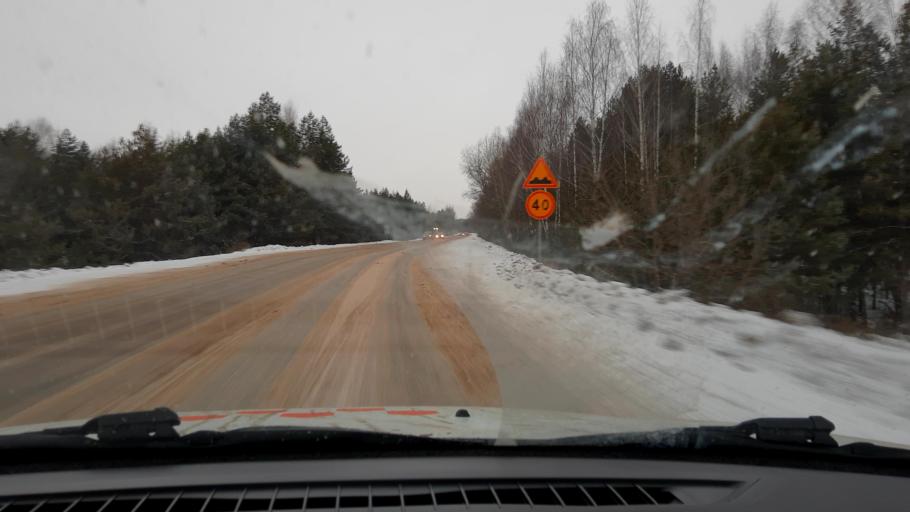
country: RU
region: Nizjnij Novgorod
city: Afonino
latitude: 56.3205
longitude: 44.1527
